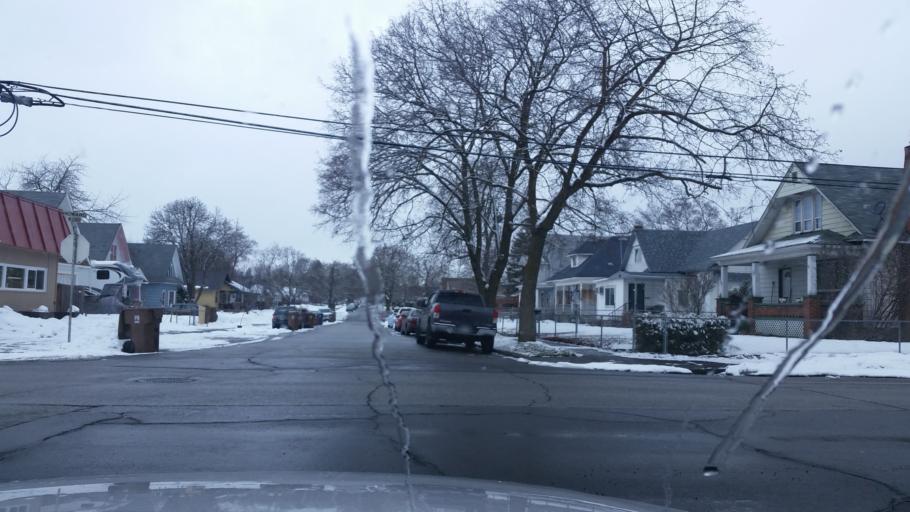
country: US
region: Washington
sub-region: Spokane County
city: Spokane
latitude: 47.6777
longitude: -117.4203
